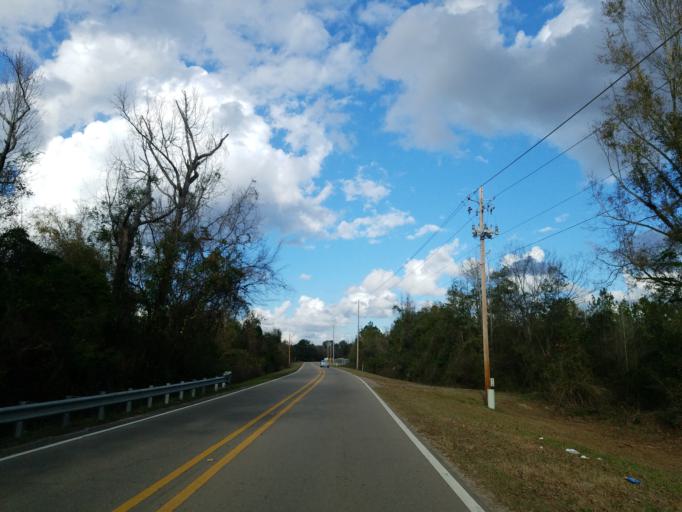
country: US
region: Mississippi
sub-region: Forrest County
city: Glendale
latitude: 31.3516
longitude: -89.3055
